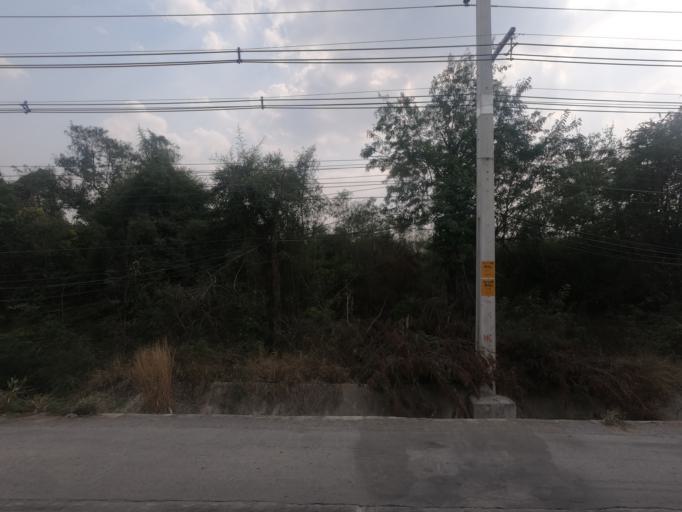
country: TH
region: Nakhon Ratchasima
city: Sikhio
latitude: 14.8697
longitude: 101.7590
